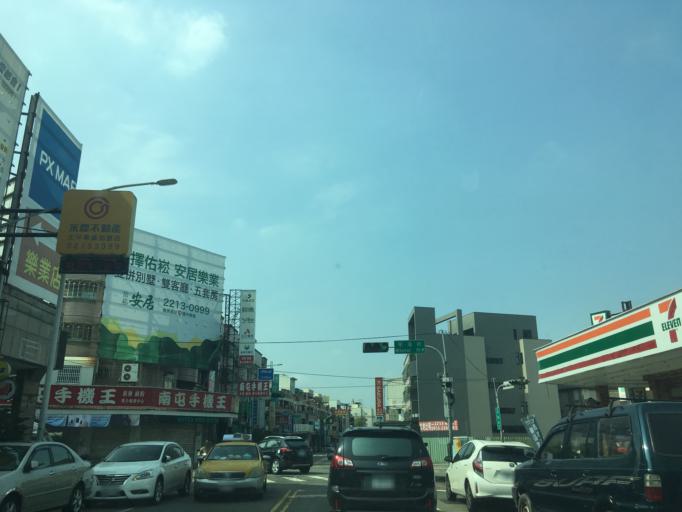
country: TW
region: Taiwan
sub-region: Taichung City
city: Taichung
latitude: 24.1410
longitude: 120.7082
